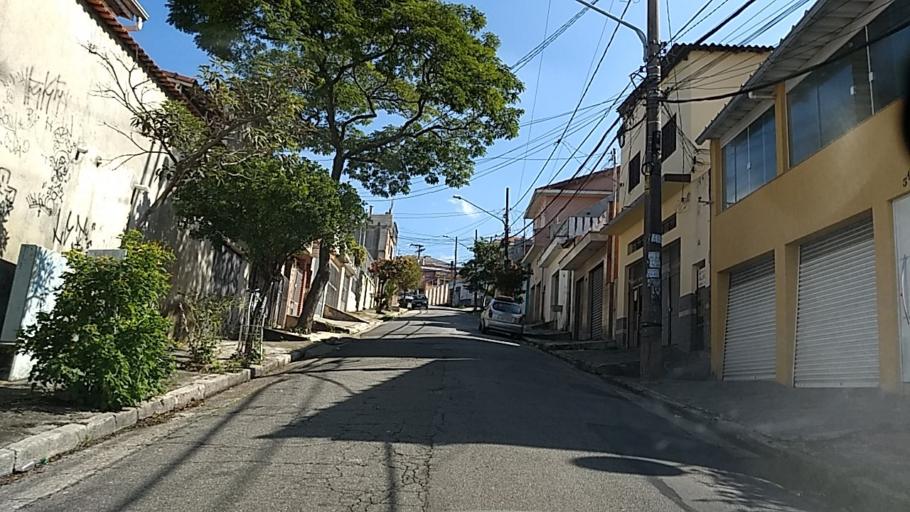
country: BR
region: Sao Paulo
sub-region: Guarulhos
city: Guarulhos
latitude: -23.4825
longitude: -46.5944
